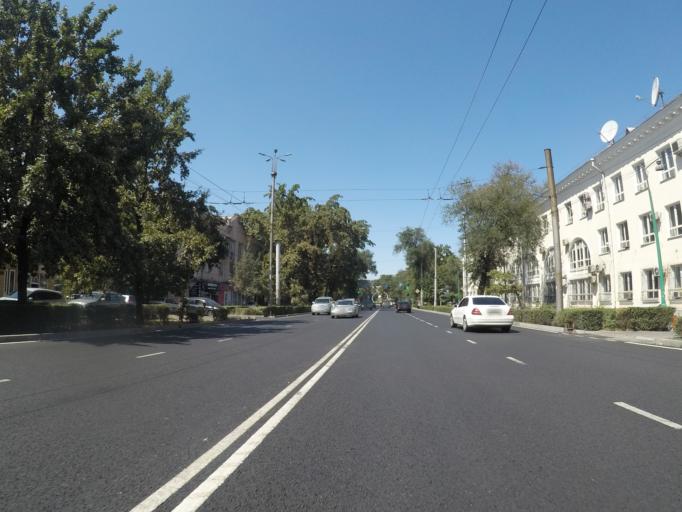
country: KG
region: Chuy
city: Bishkek
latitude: 42.8768
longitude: 74.5828
